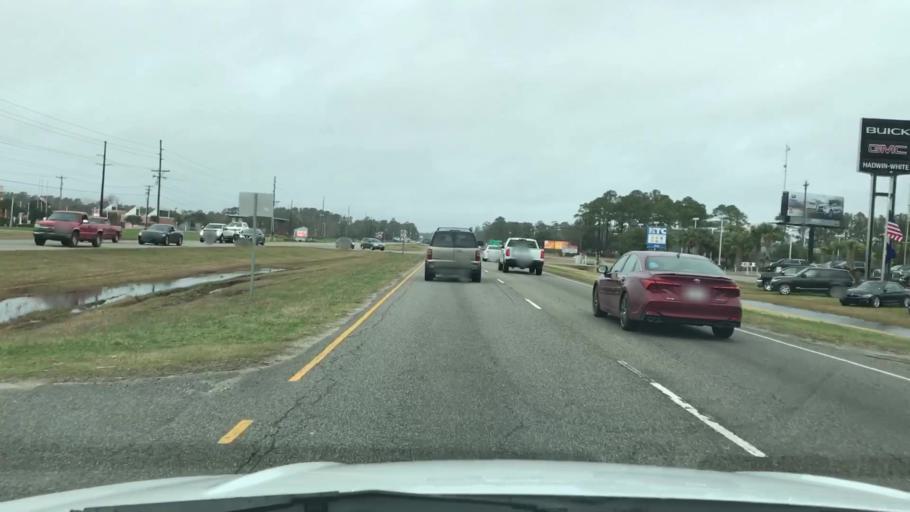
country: US
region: South Carolina
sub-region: Horry County
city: Red Hill
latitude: 33.7936
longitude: -78.9994
